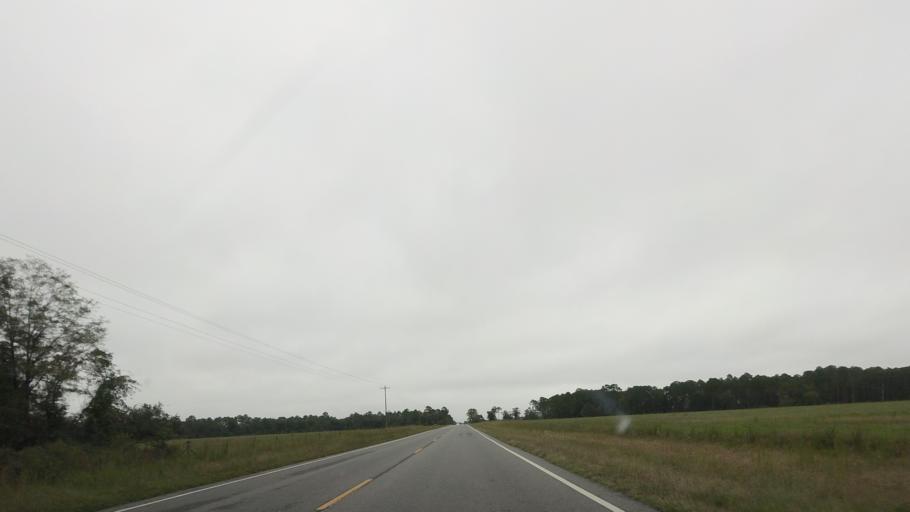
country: US
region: Georgia
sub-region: Berrien County
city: Enigma
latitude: 31.3438
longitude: -83.2287
